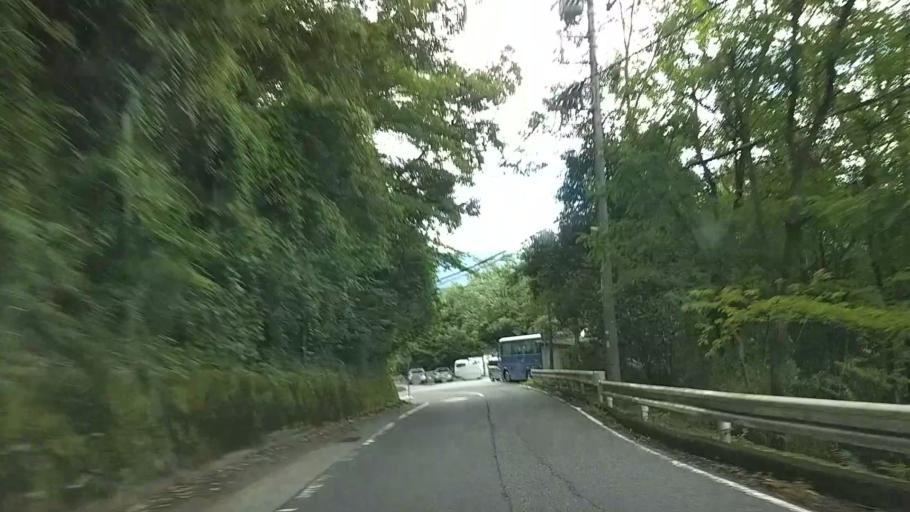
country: JP
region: Yamanashi
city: Uenohara
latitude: 35.5994
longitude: 139.1522
